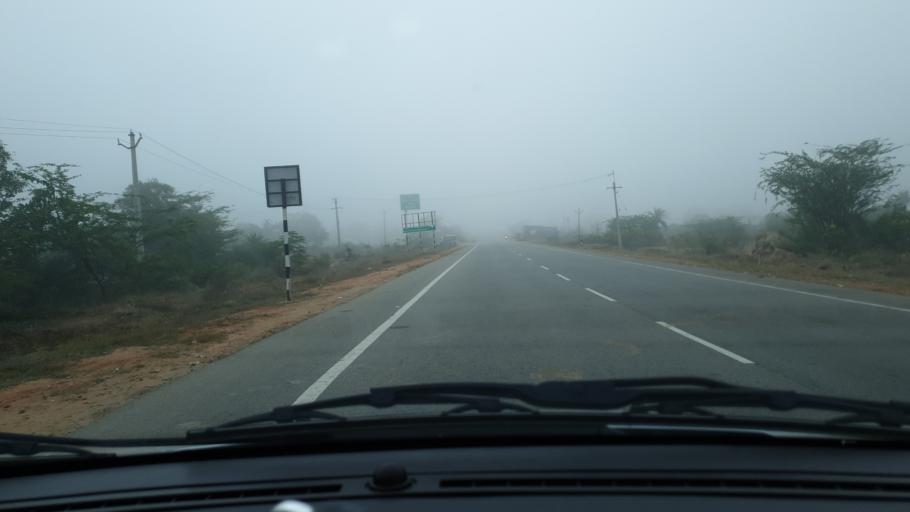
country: IN
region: Telangana
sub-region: Nalgonda
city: Devarkonda
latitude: 16.6215
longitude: 78.6719
